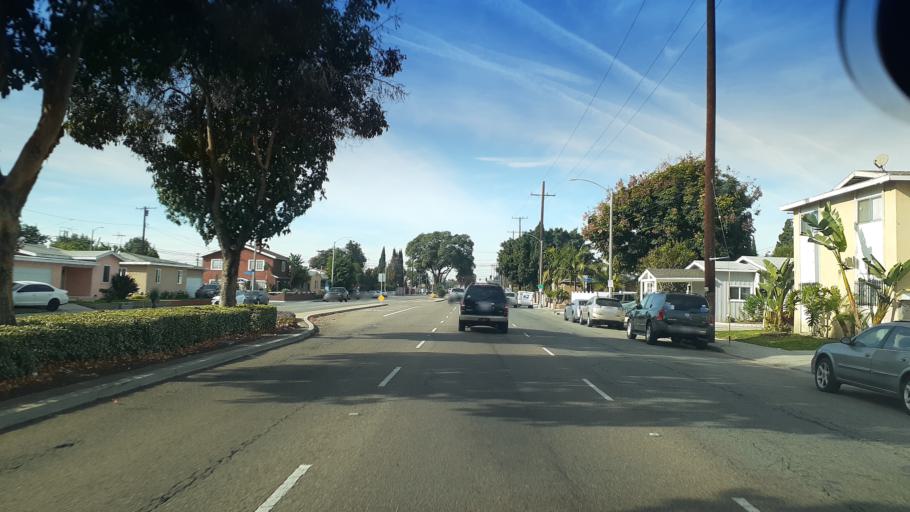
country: US
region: California
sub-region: Los Angeles County
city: Signal Hill
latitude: 33.8467
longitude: -118.1960
